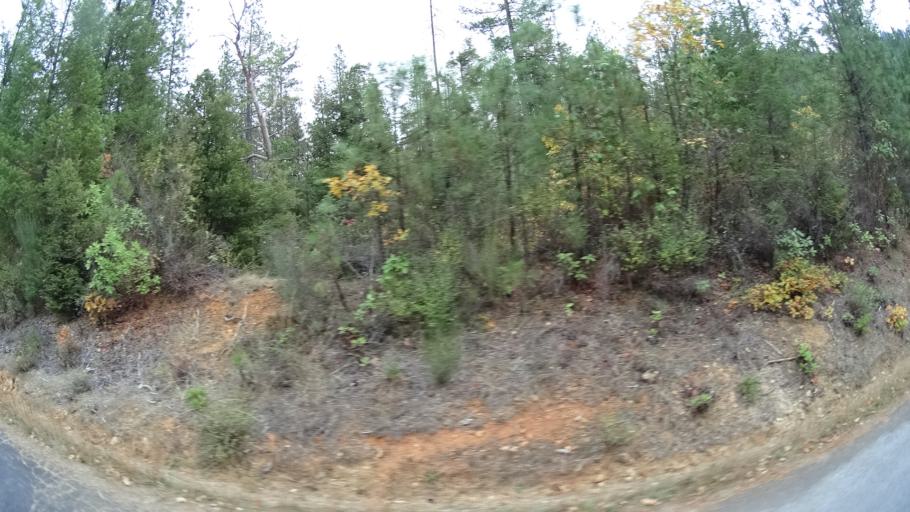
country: US
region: California
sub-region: Siskiyou County
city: Happy Camp
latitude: 41.8327
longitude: -123.1793
